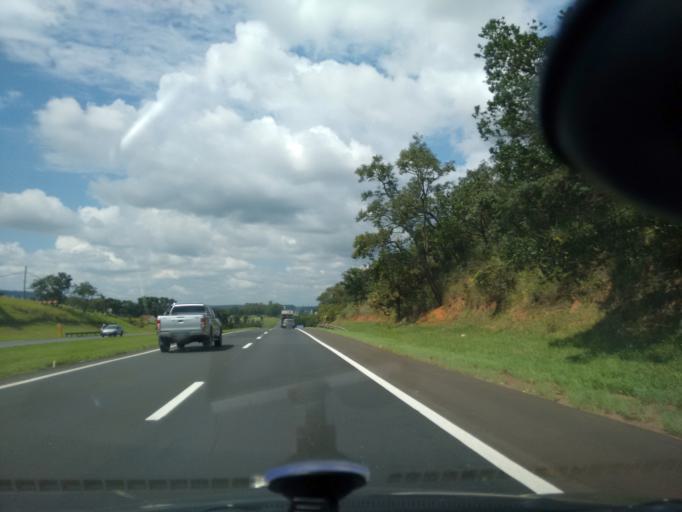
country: BR
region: Sao Paulo
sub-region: Sao Carlos
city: Sao Carlos
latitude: -22.0831
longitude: -47.8376
